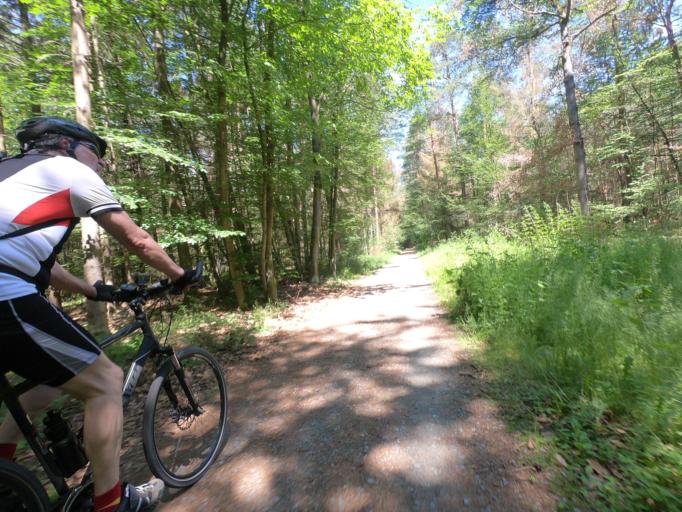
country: DE
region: Hesse
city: Heusenstamm
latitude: 50.0517
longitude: 8.7745
